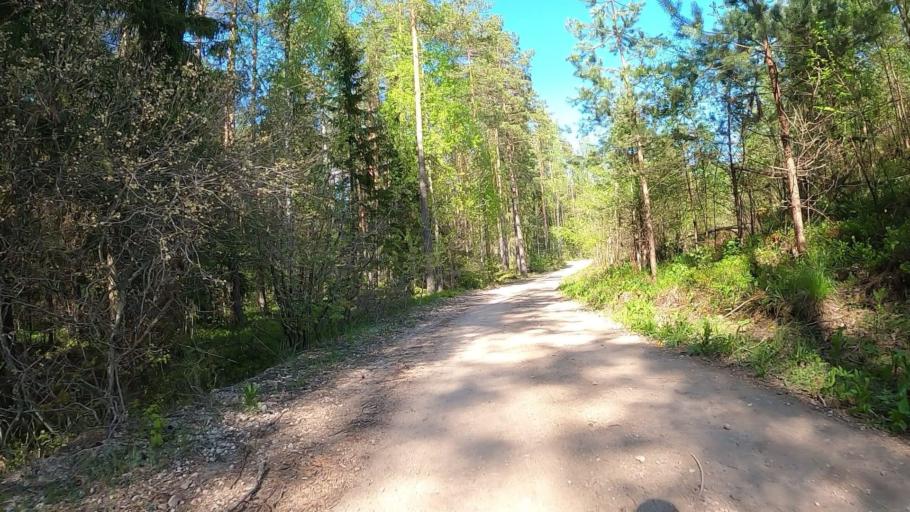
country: LV
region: Salaspils
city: Salaspils
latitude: 56.7901
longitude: 24.3293
